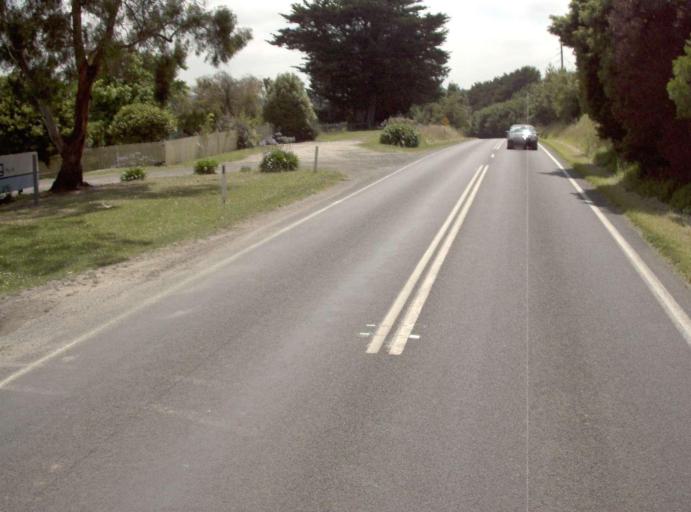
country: AU
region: Victoria
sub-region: Baw Baw
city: Warragul
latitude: -38.4662
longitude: 145.9632
